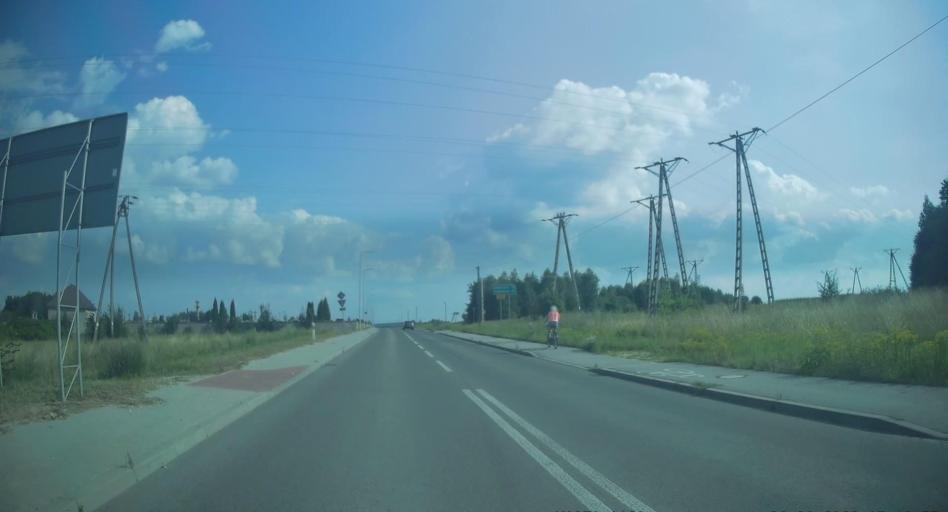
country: PL
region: Swietokrzyskie
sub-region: Powiat konecki
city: Radoszyce
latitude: 51.0702
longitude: 20.2692
